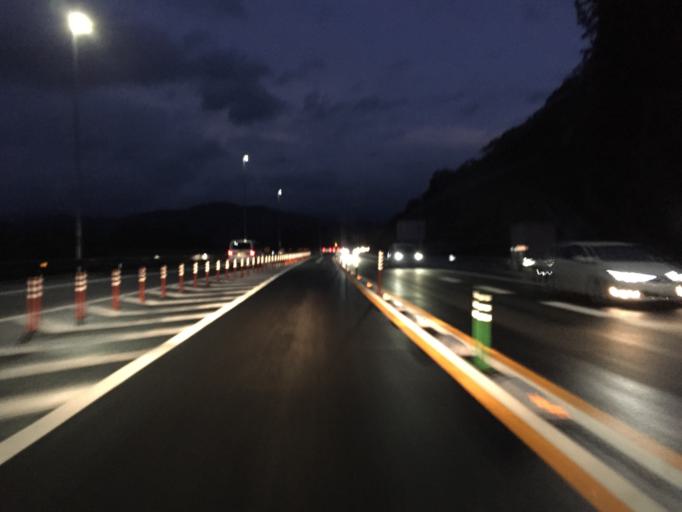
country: JP
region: Yamagata
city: Yonezawa
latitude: 37.8944
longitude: 140.1584
